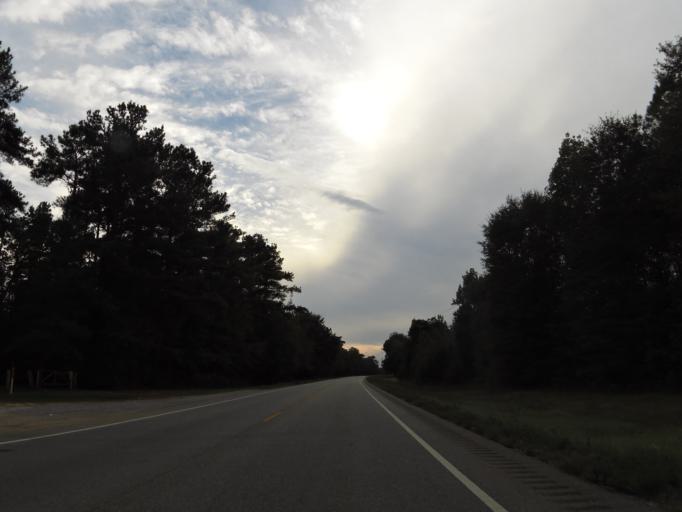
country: US
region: Alabama
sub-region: Monroe County
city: Frisco City
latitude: 31.3161
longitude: -87.4749
